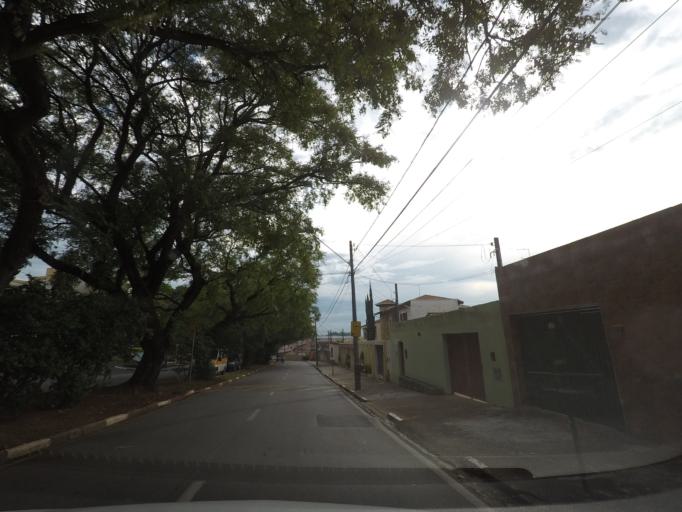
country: BR
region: Sao Paulo
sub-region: Campinas
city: Campinas
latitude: -22.9011
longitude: -47.1031
